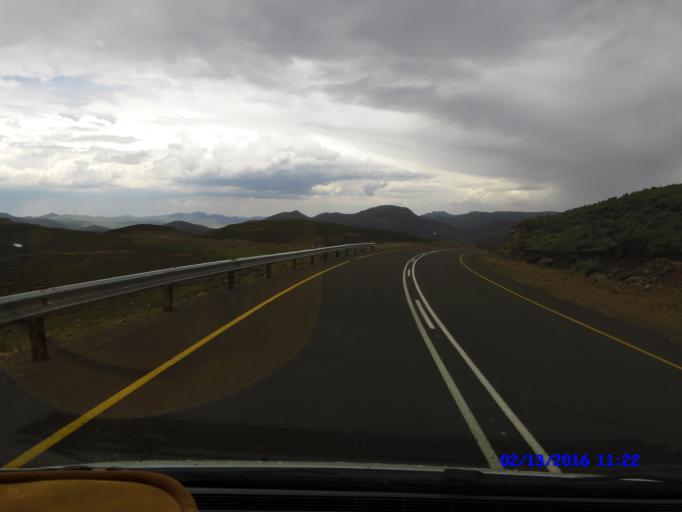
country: LS
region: Maseru
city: Nako
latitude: -29.7564
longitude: 27.9794
